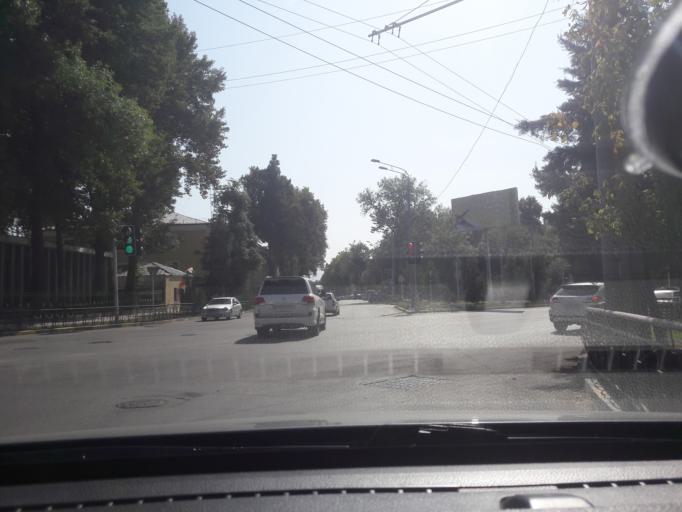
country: TJ
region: Dushanbe
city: Dushanbe
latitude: 38.5726
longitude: 68.8000
